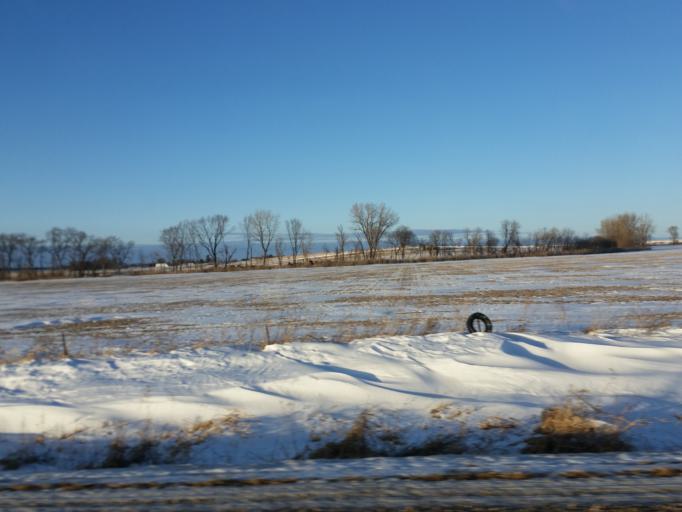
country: US
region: Iowa
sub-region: Butler County
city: Allison
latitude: 42.7448
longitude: -92.9006
